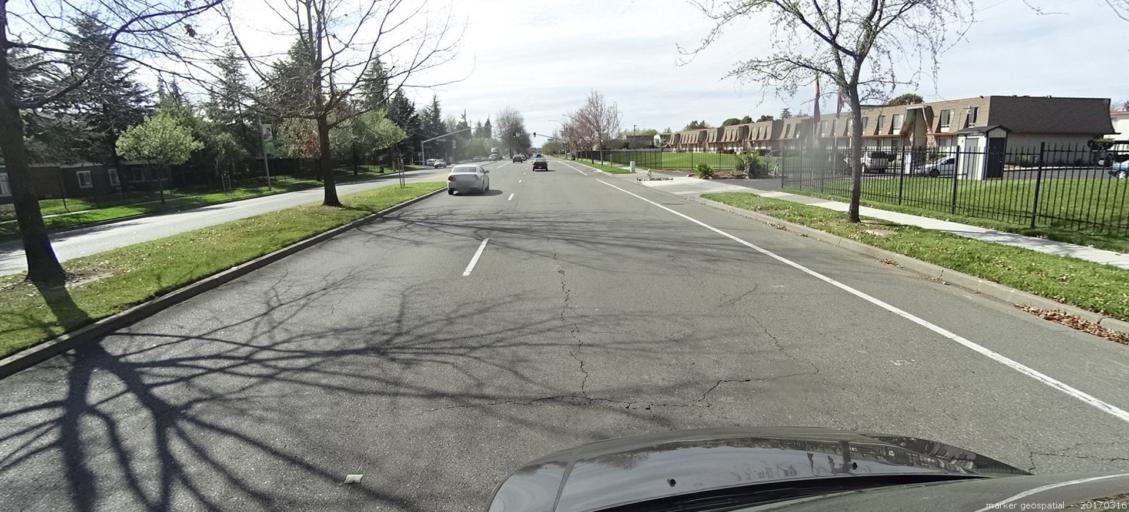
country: US
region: California
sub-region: Sacramento County
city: Parkway
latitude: 38.4743
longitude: -121.4401
